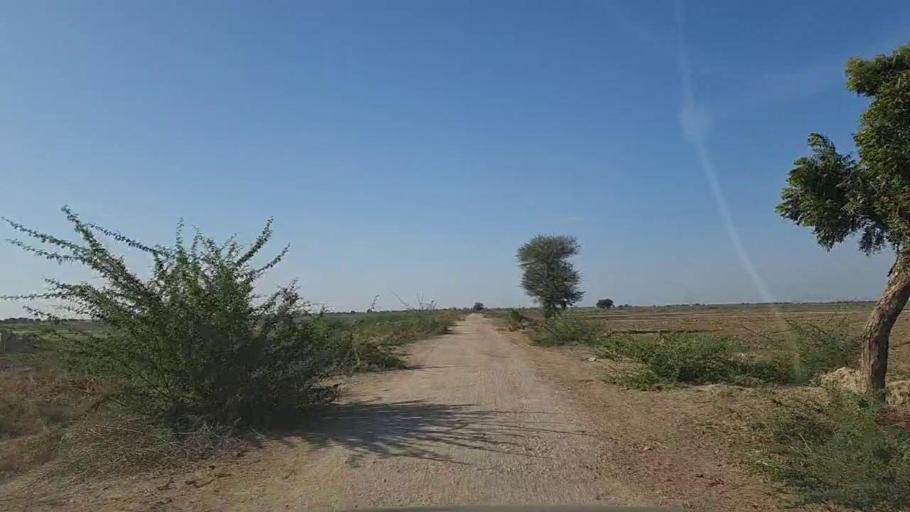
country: PK
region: Sindh
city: Kunri
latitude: 25.2307
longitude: 69.5059
